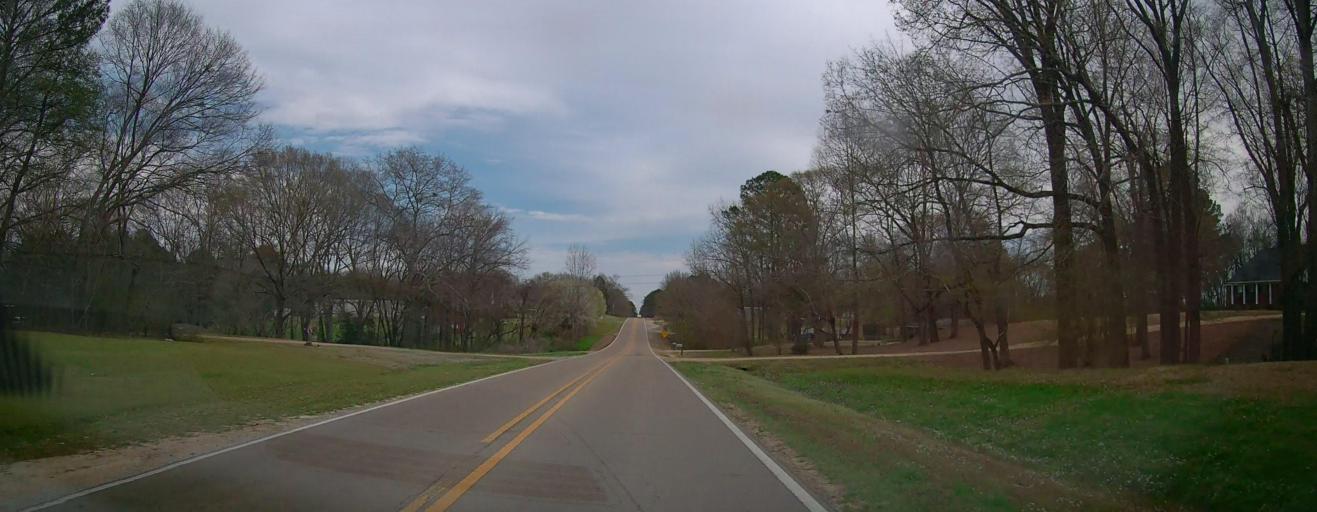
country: US
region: Mississippi
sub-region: Itawamba County
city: Mantachie
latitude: 34.2594
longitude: -88.5147
